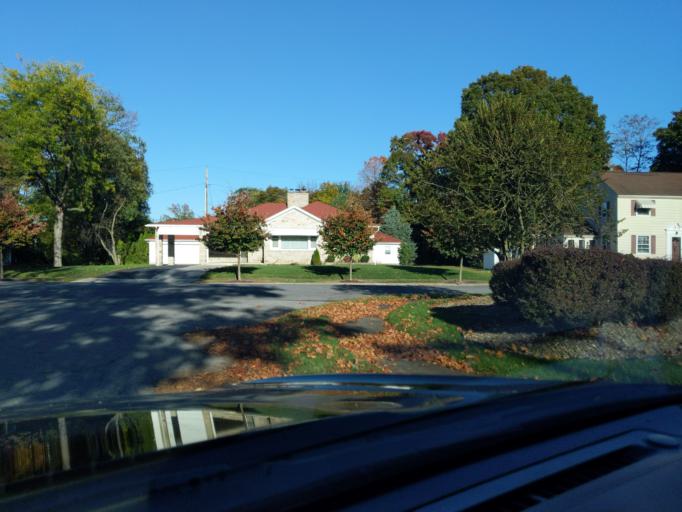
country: US
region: Pennsylvania
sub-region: Blair County
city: Lakemont
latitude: 40.4816
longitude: -78.4045
